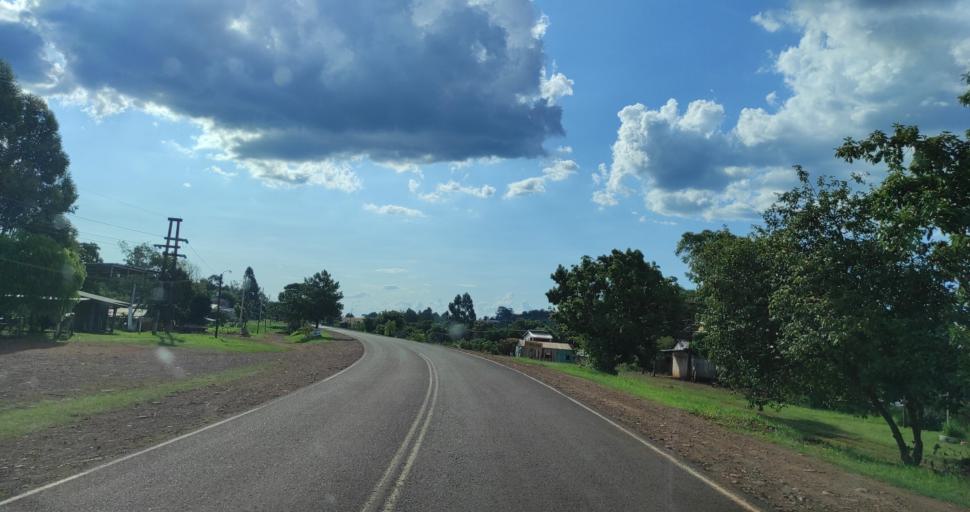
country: AR
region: Misiones
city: San Vicente
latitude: -26.3429
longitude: -54.1582
